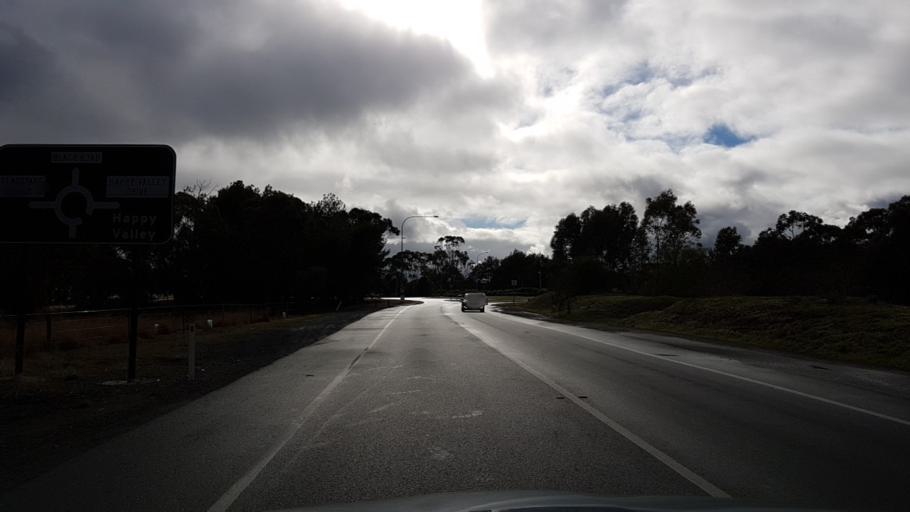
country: AU
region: South Australia
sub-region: Onkaparinga
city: Bedford Park
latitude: -35.0521
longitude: 138.5720
